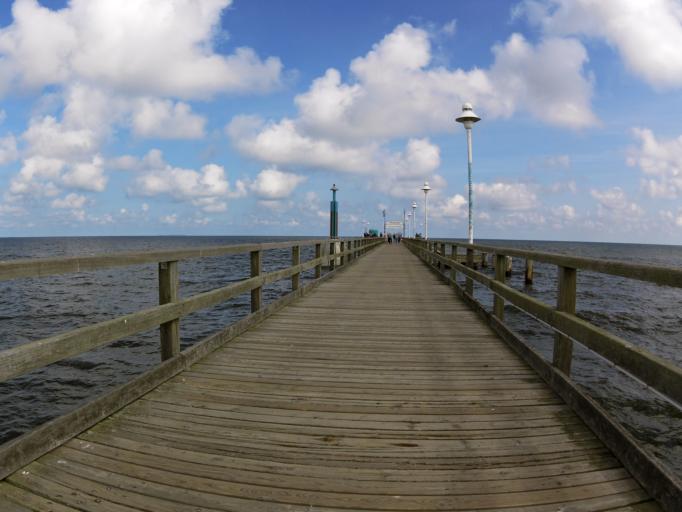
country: DE
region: Mecklenburg-Vorpommern
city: Ostseebad Zinnowitz
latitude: 54.0834
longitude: 13.9167
